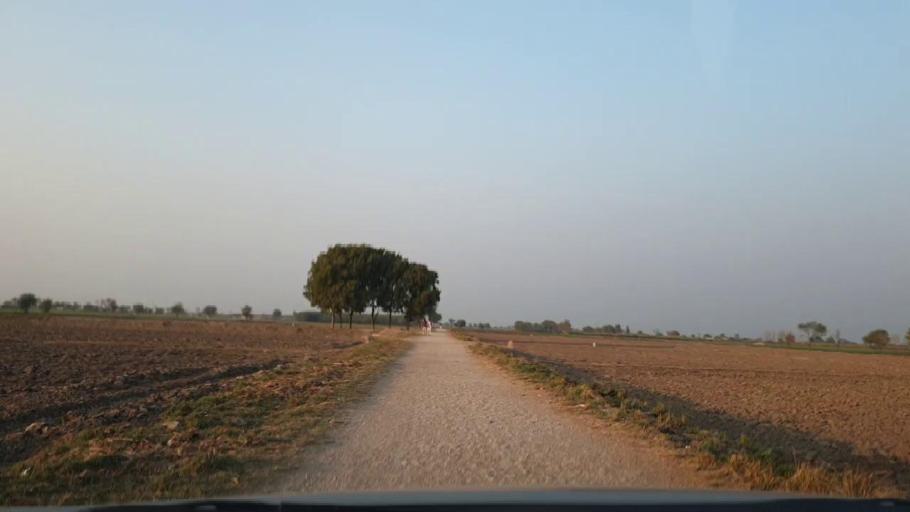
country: PK
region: Sindh
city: Tando Adam
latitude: 25.7134
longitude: 68.5792
